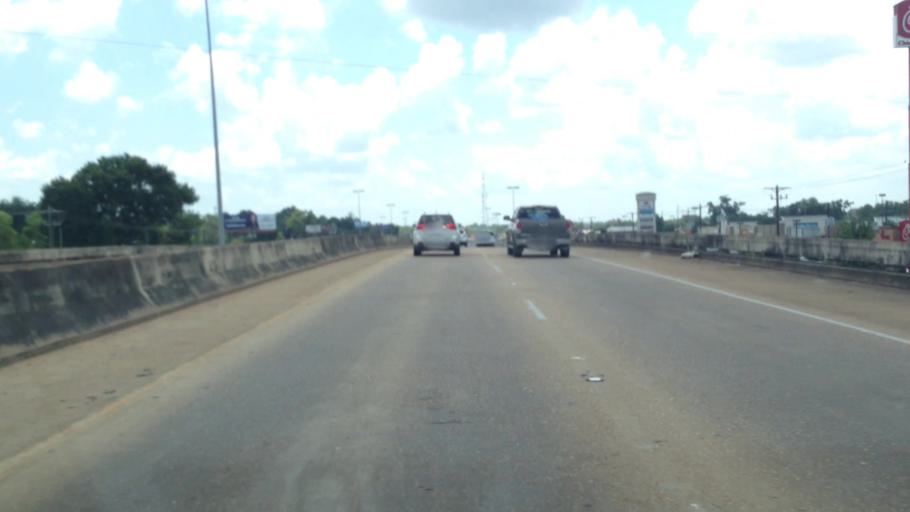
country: US
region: Louisiana
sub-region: Rapides Parish
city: Alexandria
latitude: 31.2866
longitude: -92.4750
